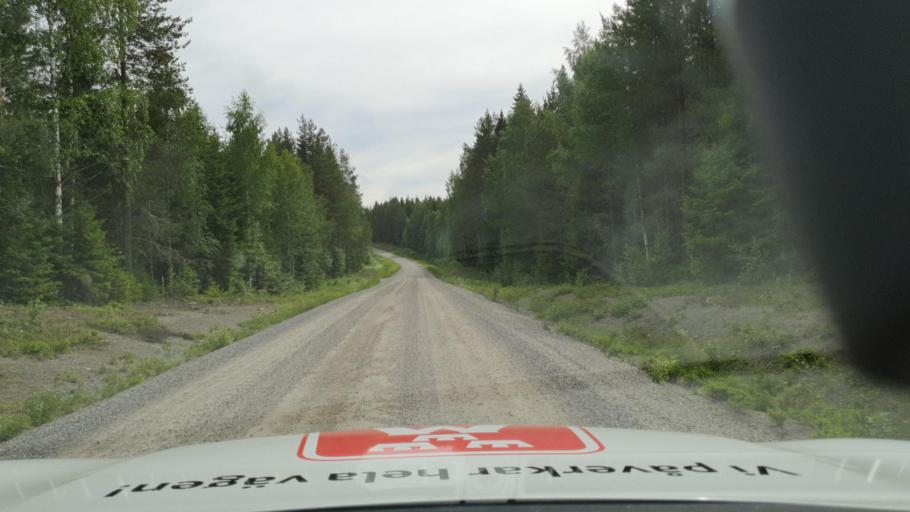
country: SE
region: Vaesterbotten
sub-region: Skelleftea Kommun
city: Burea
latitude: 64.4424
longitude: 21.0190
